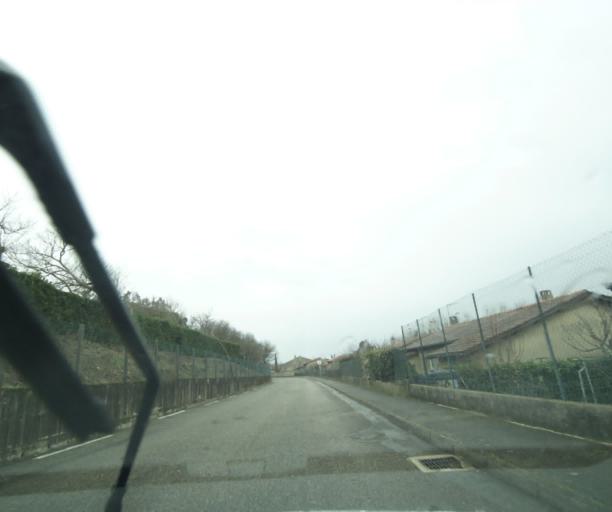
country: FR
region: Rhone-Alpes
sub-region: Departement de la Drome
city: Bourg-les-Valence
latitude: 44.9739
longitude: 4.9000
